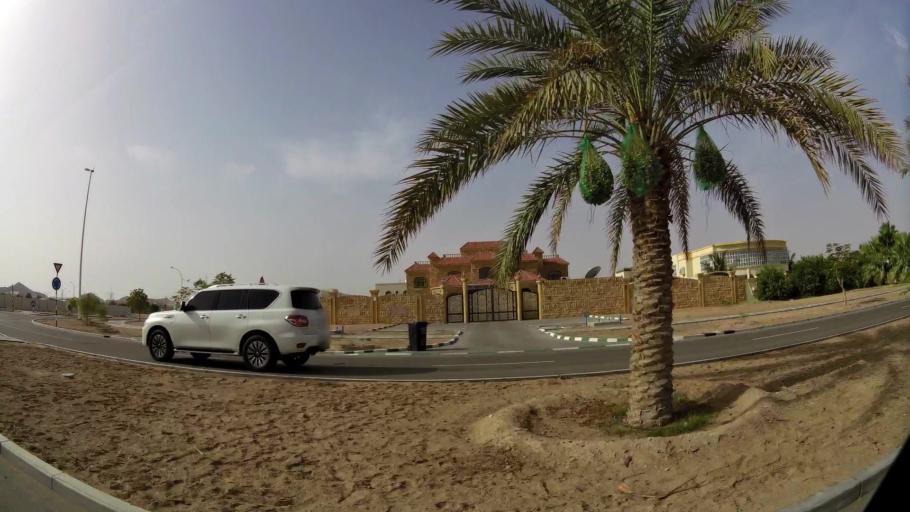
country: AE
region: Abu Dhabi
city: Al Ain
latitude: 24.1532
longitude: 55.7190
